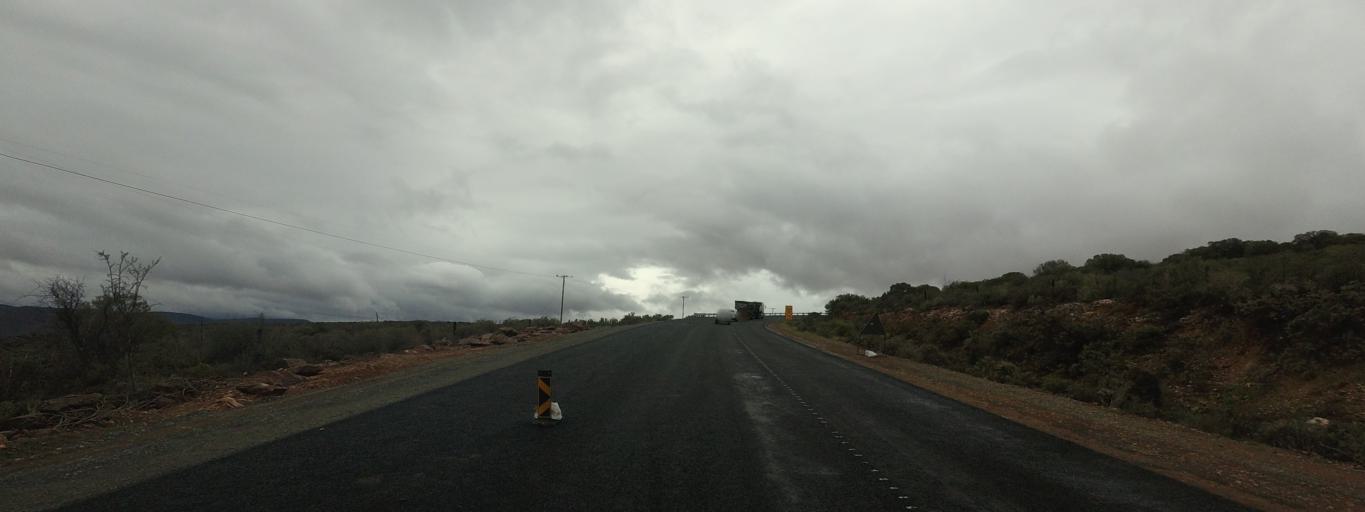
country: ZA
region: Western Cape
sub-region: Eden District Municipality
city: Oudtshoorn
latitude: -33.7223
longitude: 22.3052
